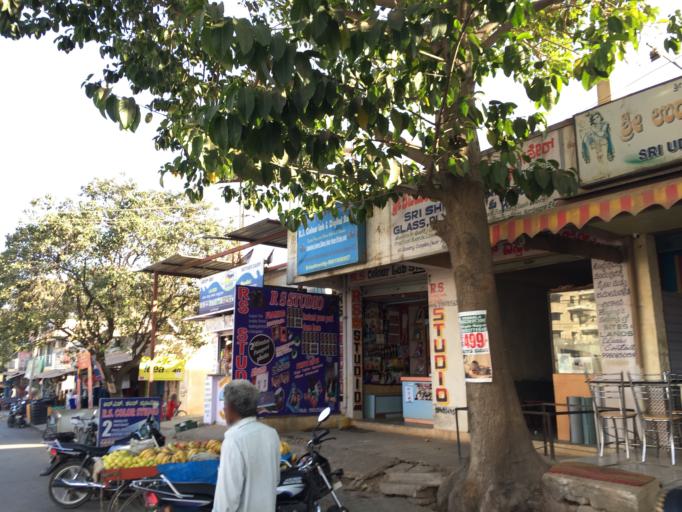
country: IN
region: Karnataka
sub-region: Bangalore Urban
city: Yelahanka
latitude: 13.0571
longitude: 77.6282
